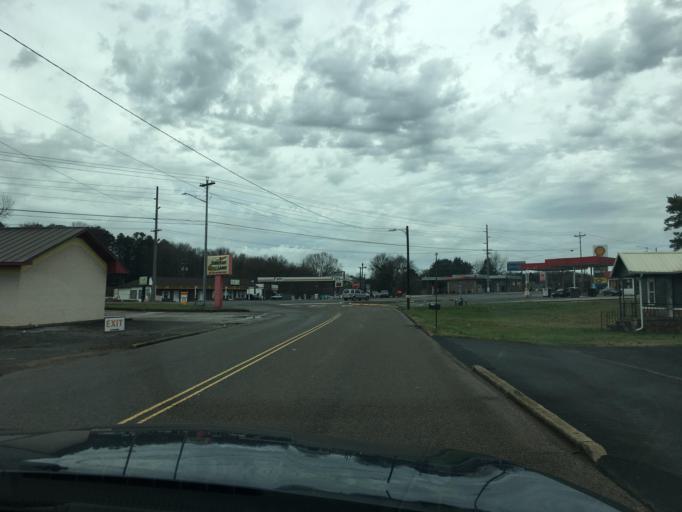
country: US
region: Tennessee
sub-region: McMinn County
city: Athens
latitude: 35.4663
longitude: -84.6062
